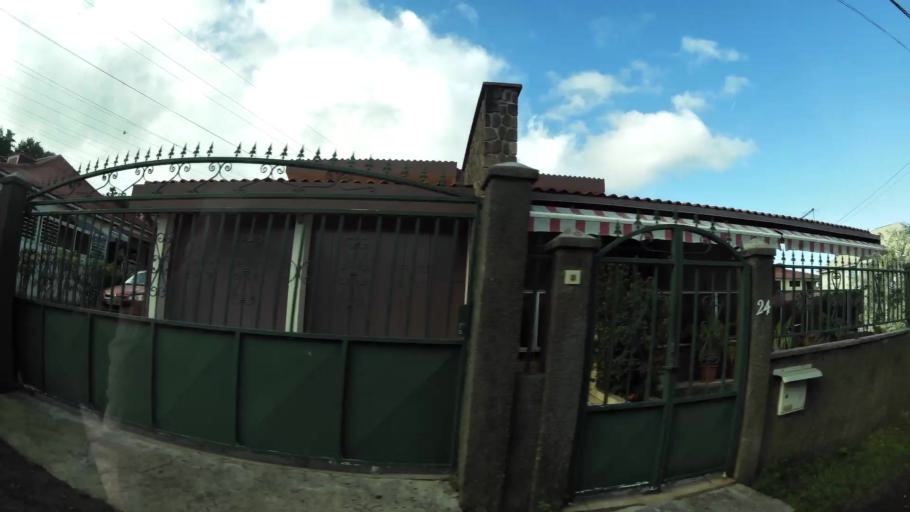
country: GP
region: Guadeloupe
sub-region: Guadeloupe
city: Les Abymes
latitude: 16.2536
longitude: -61.5124
